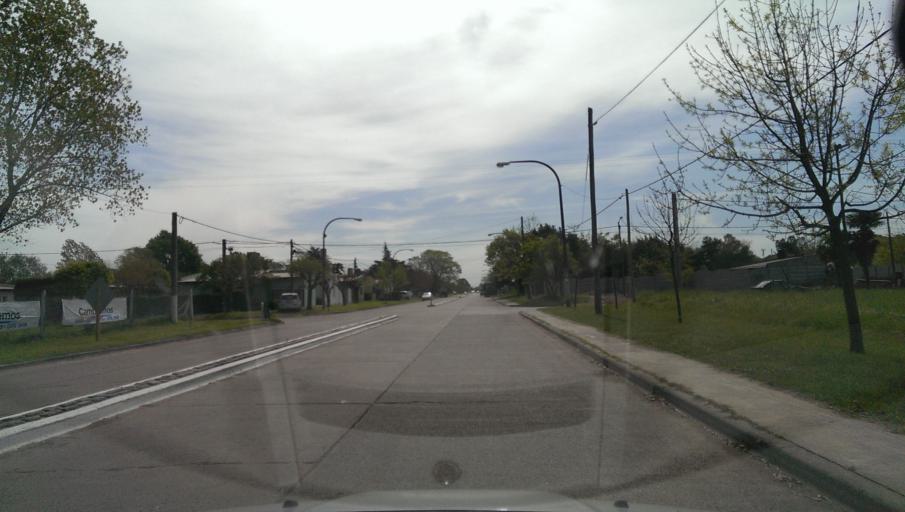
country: AR
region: Buenos Aires
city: Tapalque
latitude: -36.3867
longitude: -59.4936
